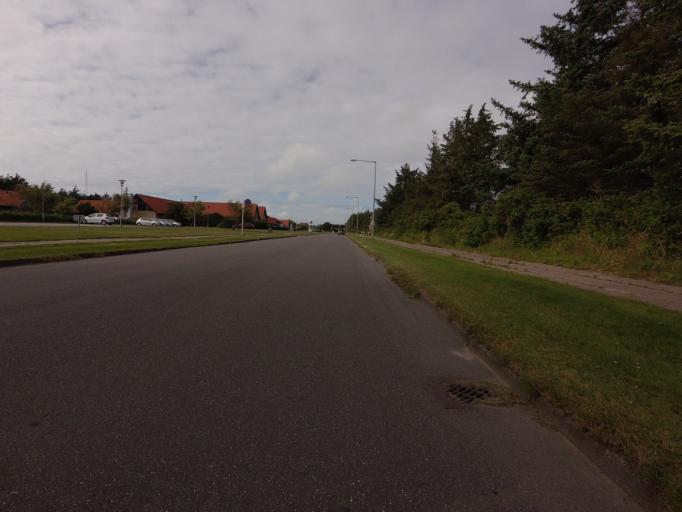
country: DK
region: North Denmark
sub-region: Jammerbugt Kommune
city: Pandrup
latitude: 57.3654
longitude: 9.7166
